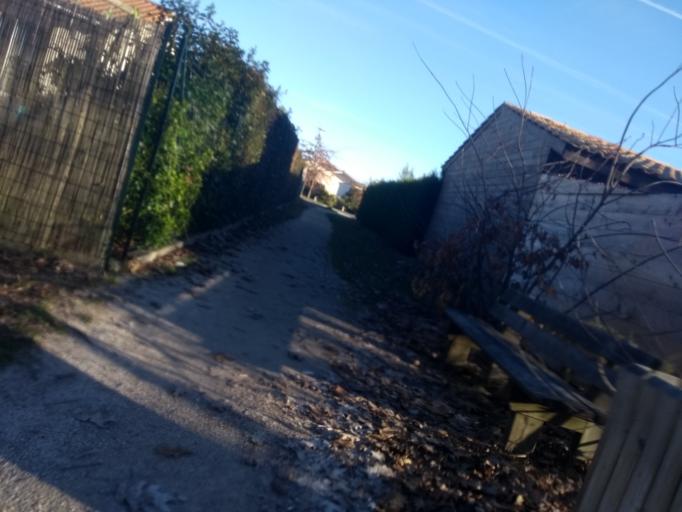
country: FR
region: Aquitaine
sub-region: Departement de la Gironde
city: Le Barp
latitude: 44.6097
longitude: -0.7825
